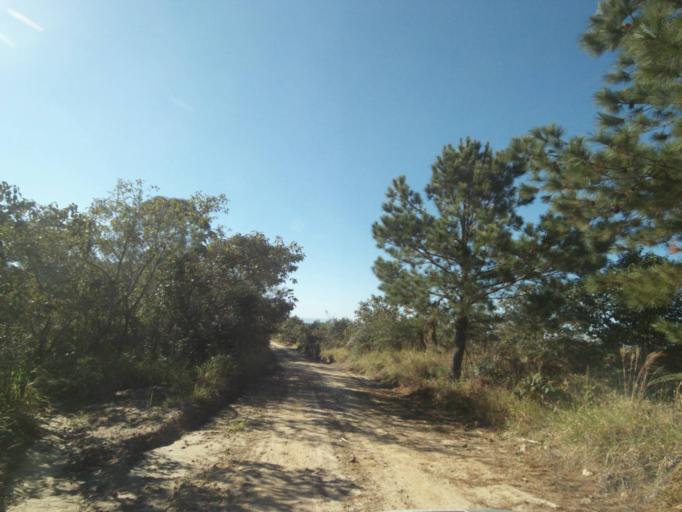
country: BR
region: Parana
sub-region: Tibagi
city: Tibagi
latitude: -24.5690
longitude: -50.4713
